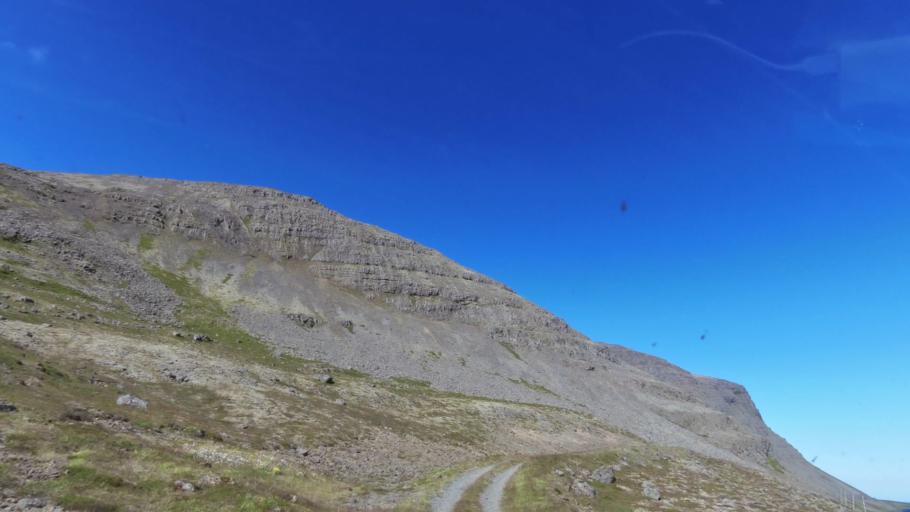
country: IS
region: West
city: Olafsvik
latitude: 65.6223
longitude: -23.8798
